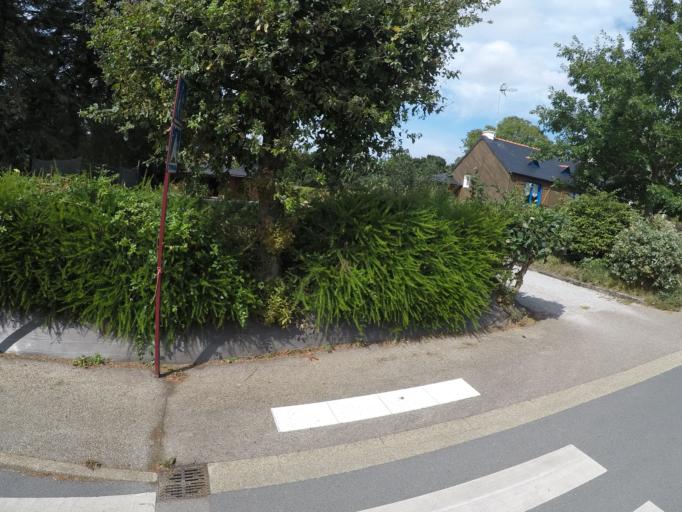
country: FR
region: Brittany
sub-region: Departement des Cotes-d'Armor
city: Goudelin
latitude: 48.6023
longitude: -3.0218
